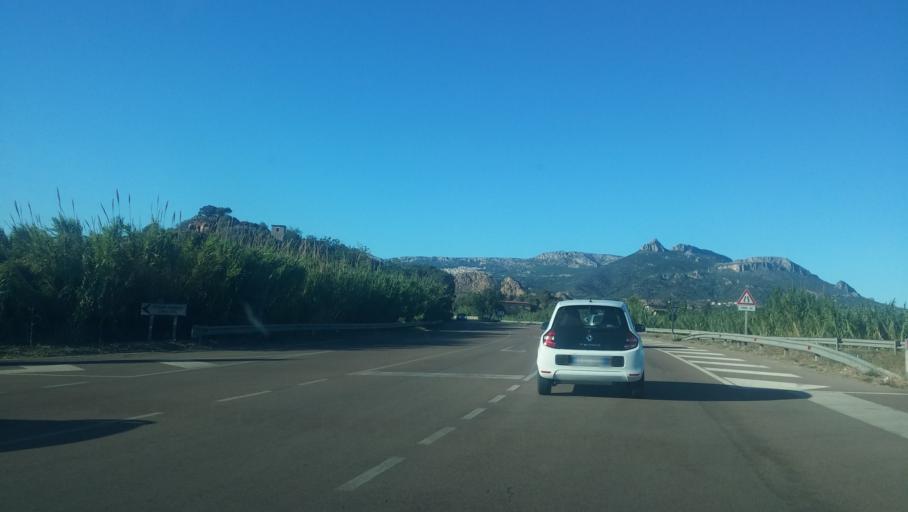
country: IT
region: Sardinia
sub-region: Provincia di Ogliastra
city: Lotzorai
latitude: 39.9615
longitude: 9.6573
